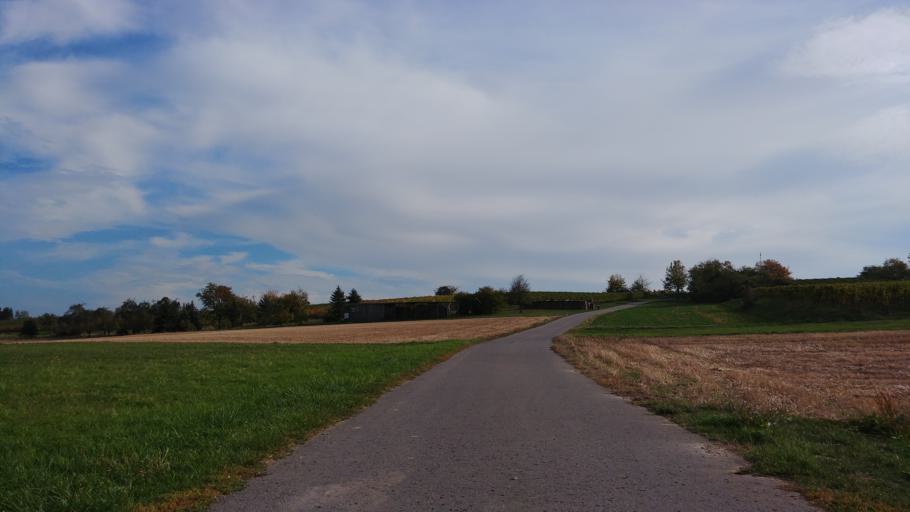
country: DE
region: Baden-Wuerttemberg
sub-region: Regierungsbezirk Stuttgart
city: Ilsfeld
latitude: 49.0717
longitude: 9.2440
